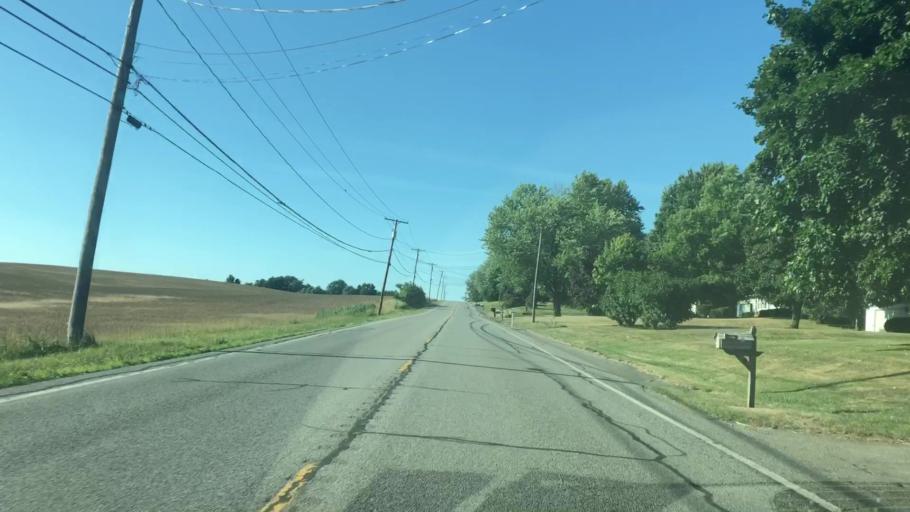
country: US
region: New York
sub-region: Wayne County
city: Macedon
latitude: 43.1335
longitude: -77.2926
